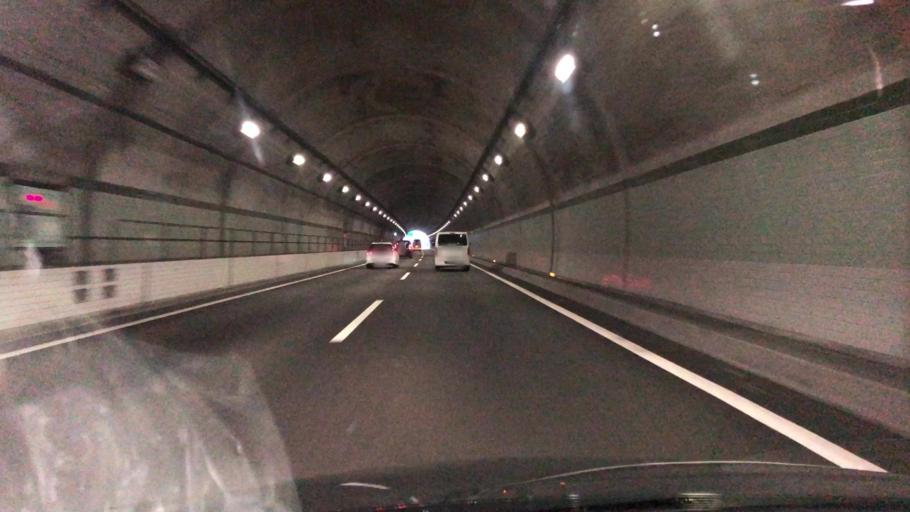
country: JP
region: Tokyo
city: Itsukaichi
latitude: 35.6729
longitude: 139.2514
